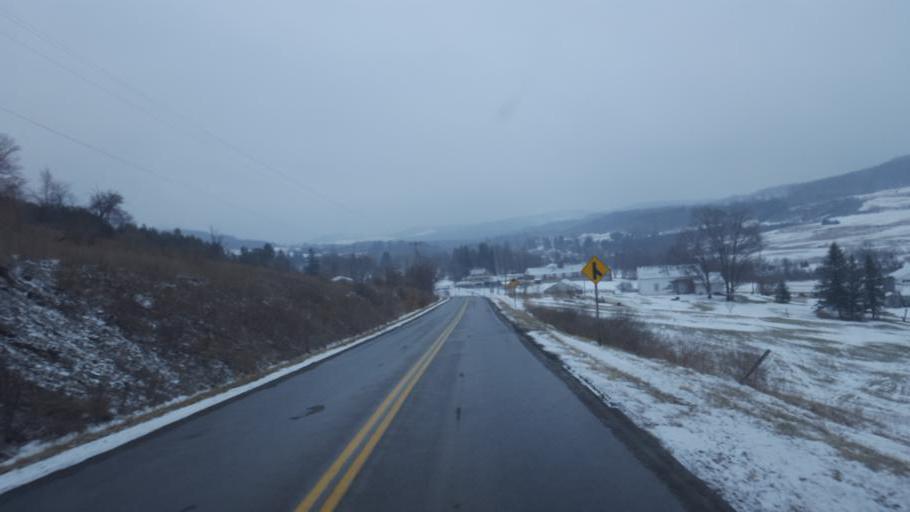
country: US
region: Pennsylvania
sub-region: Tioga County
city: Elkland
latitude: 42.0798
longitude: -77.4190
